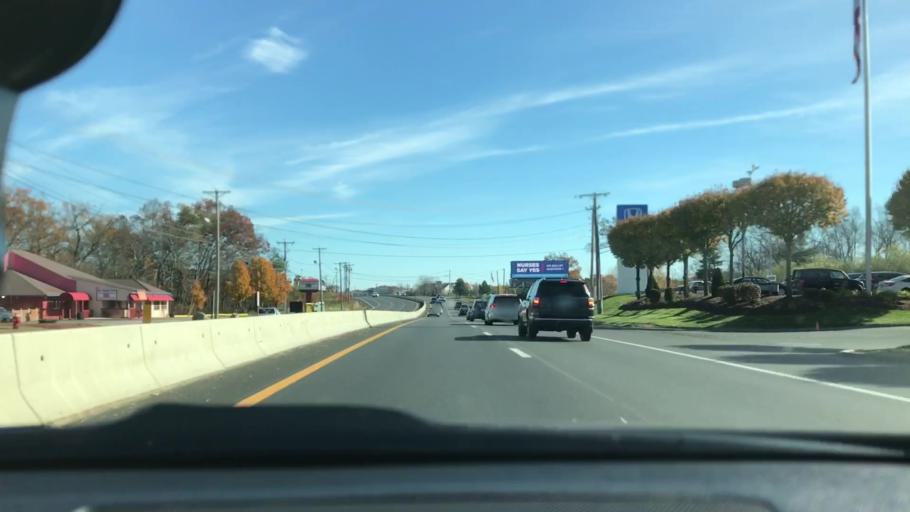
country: US
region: Massachusetts
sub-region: Worcester County
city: Northborough
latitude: 42.2829
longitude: -71.6604
